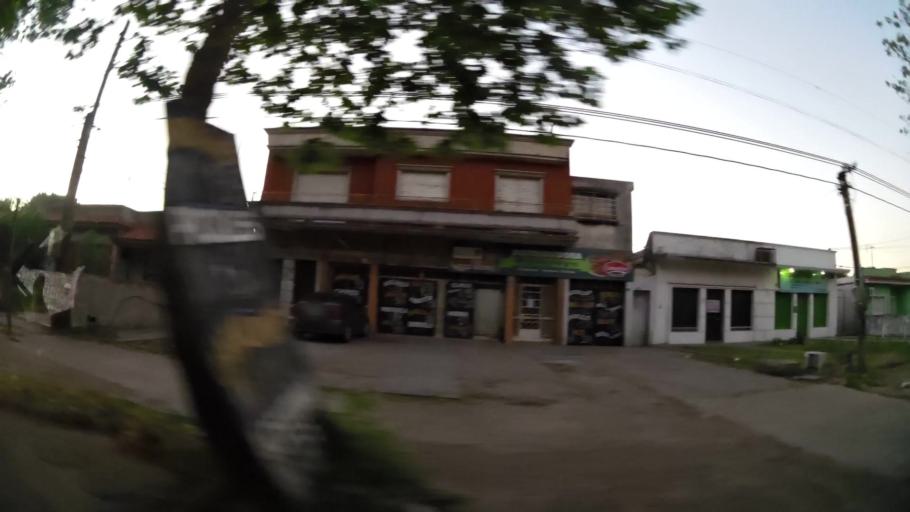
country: UY
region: Canelones
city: Toledo
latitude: -34.8201
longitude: -56.1400
